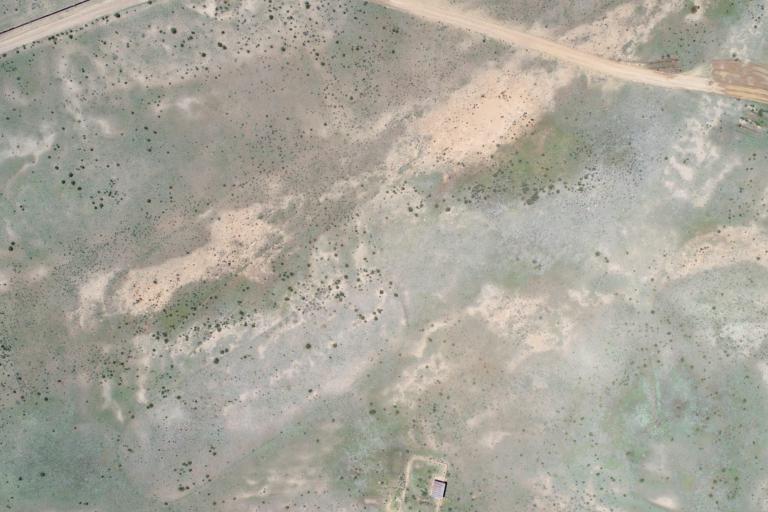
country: BO
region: La Paz
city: Curahuara de Carangas
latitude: -17.2791
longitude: -68.5175
